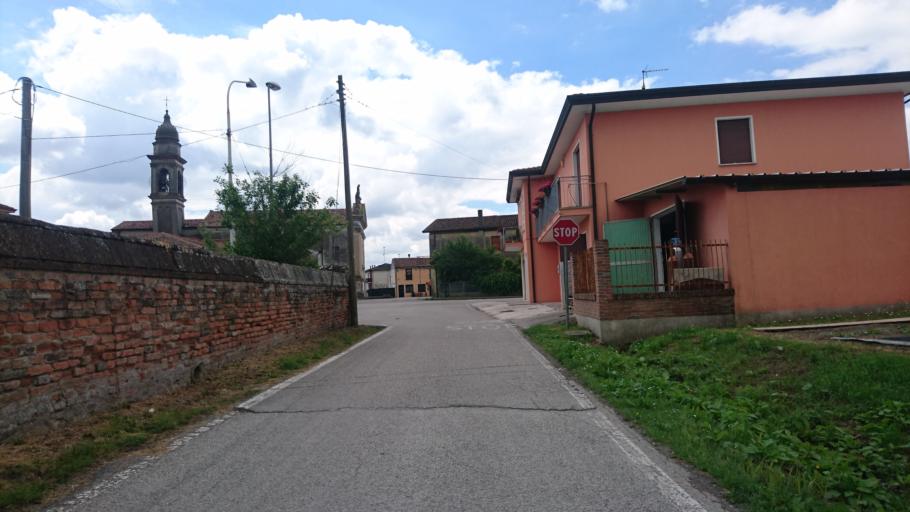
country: IT
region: Veneto
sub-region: Provincia di Padova
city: Villa Estense
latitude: 45.1502
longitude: 11.6494
